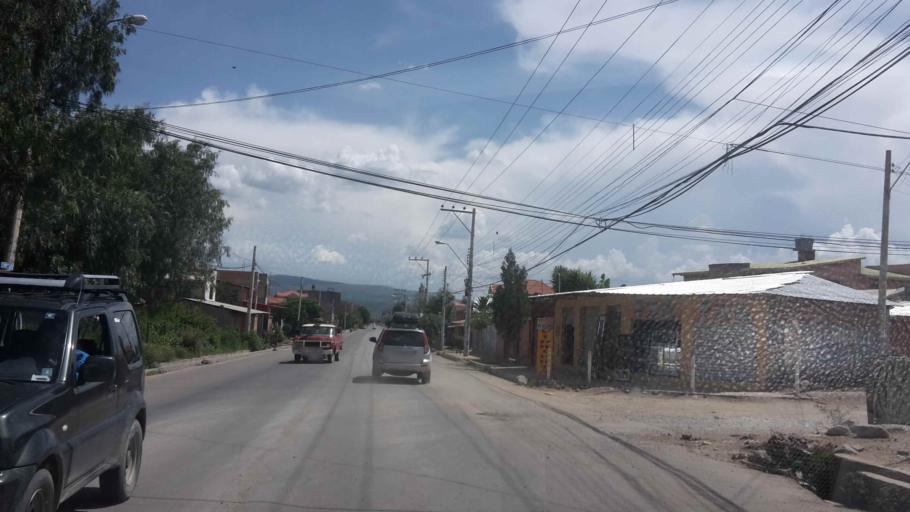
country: BO
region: Cochabamba
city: Cochabamba
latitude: -17.3683
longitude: -66.2313
